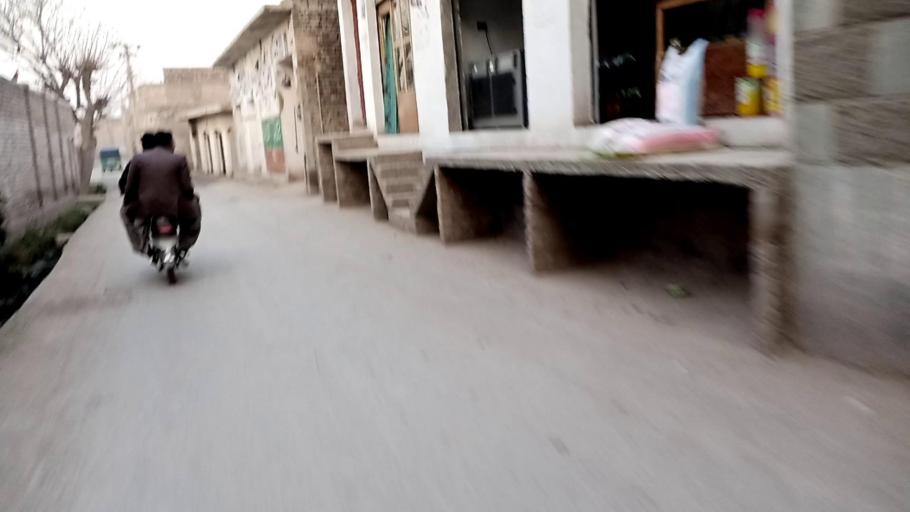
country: PK
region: Khyber Pakhtunkhwa
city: Peshawar
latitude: 34.0307
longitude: 71.4906
